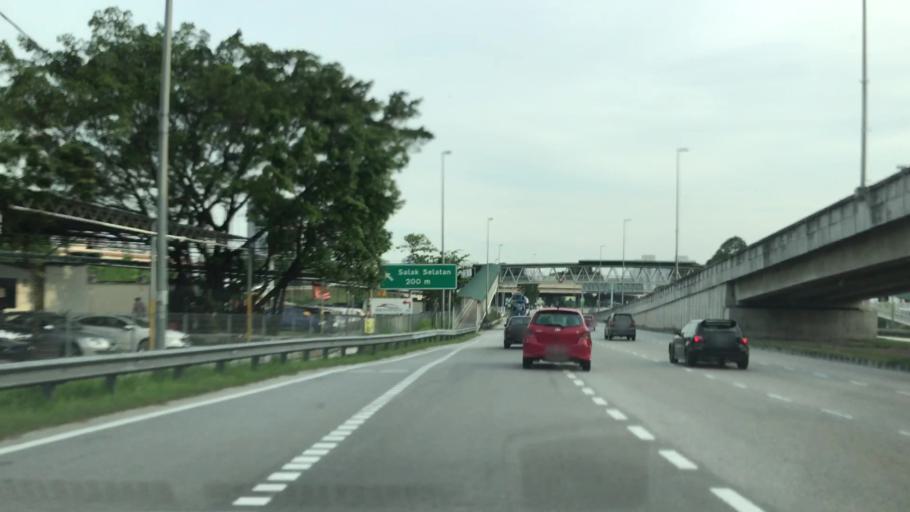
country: MY
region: Kuala Lumpur
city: Kuala Lumpur
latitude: 3.1075
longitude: 101.7074
